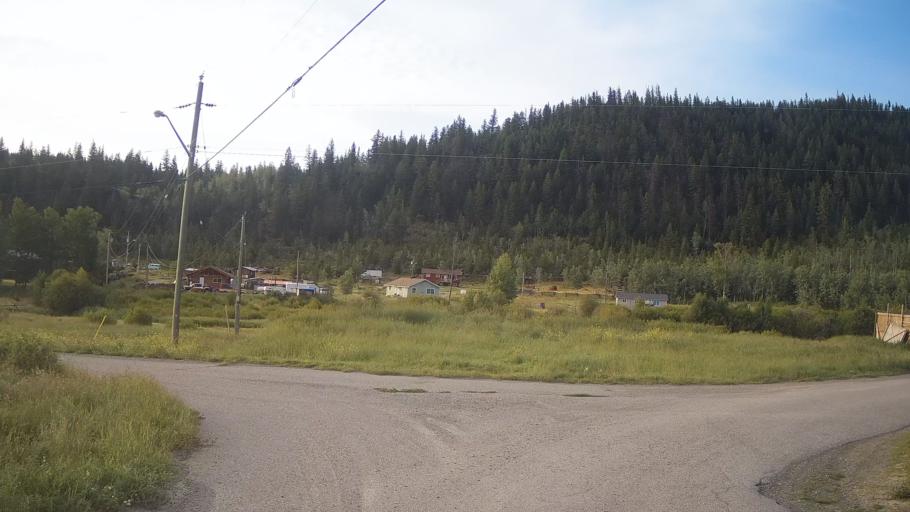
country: CA
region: British Columbia
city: Hanceville
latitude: 52.1369
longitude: -123.9505
